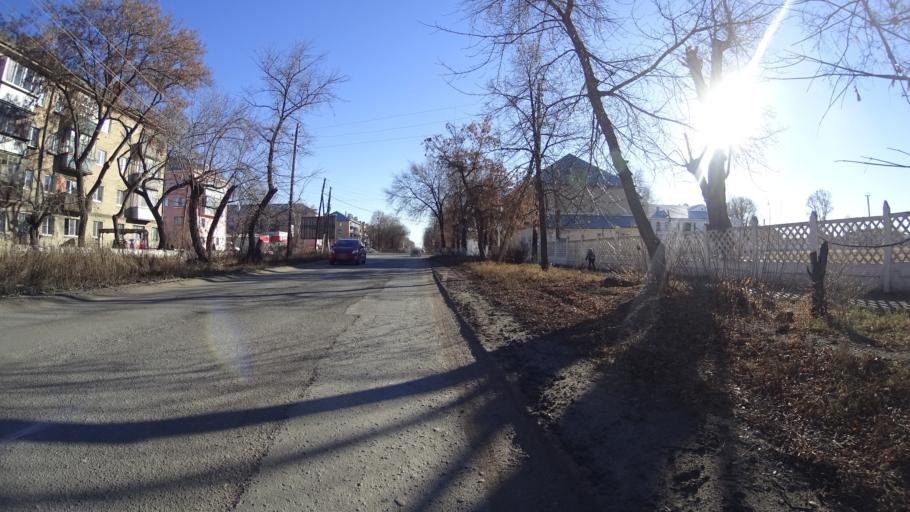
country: RU
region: Chelyabinsk
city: Troitsk
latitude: 54.1131
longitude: 61.5665
